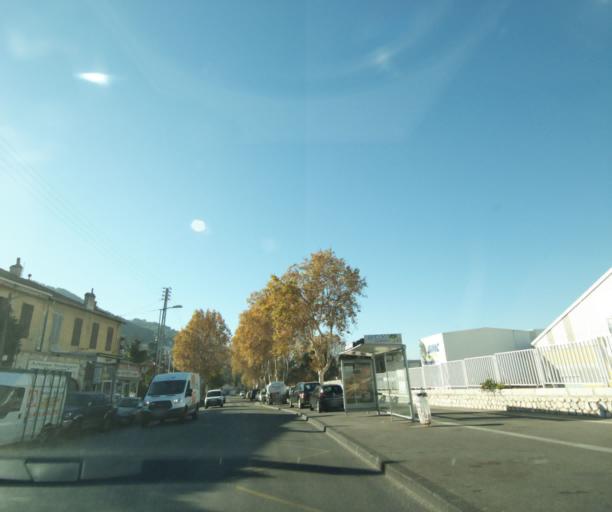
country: FR
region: Provence-Alpes-Cote d'Azur
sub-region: Departement des Bouches-du-Rhone
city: La Penne-sur-Huveaune
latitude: 43.2838
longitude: 5.4987
